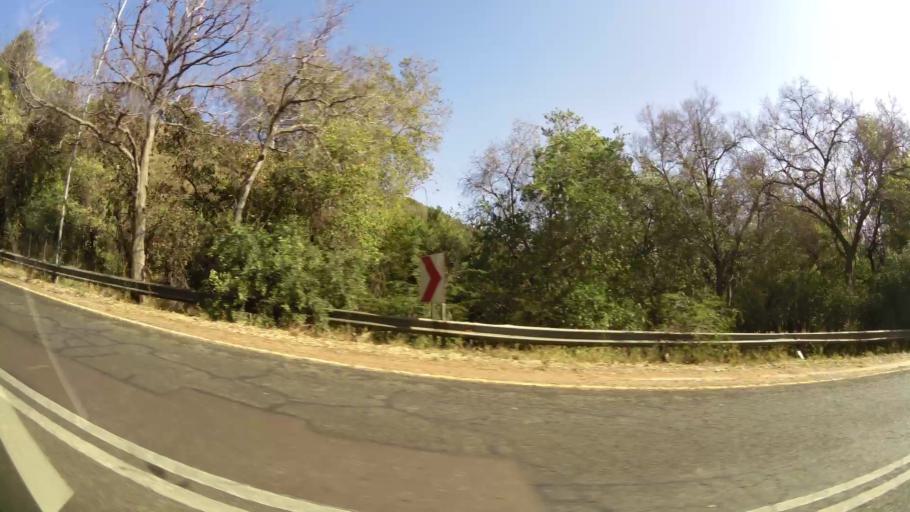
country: ZA
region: Gauteng
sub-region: City of Tshwane Metropolitan Municipality
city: Pretoria
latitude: -25.6875
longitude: 28.1930
